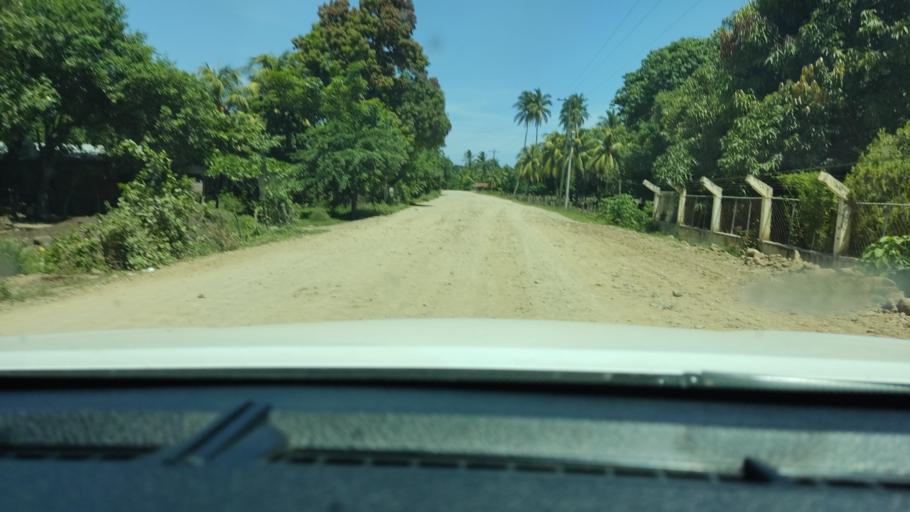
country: SV
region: Ahuachapan
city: San Francisco Menendez
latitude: 13.7796
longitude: -90.1154
